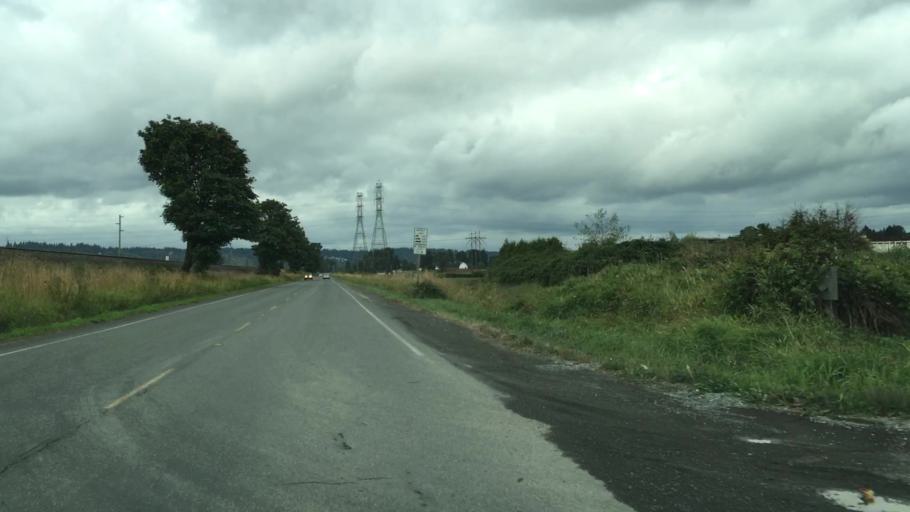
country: US
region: Washington
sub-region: Snohomish County
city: Snohomish
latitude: 47.9161
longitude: -122.1313
